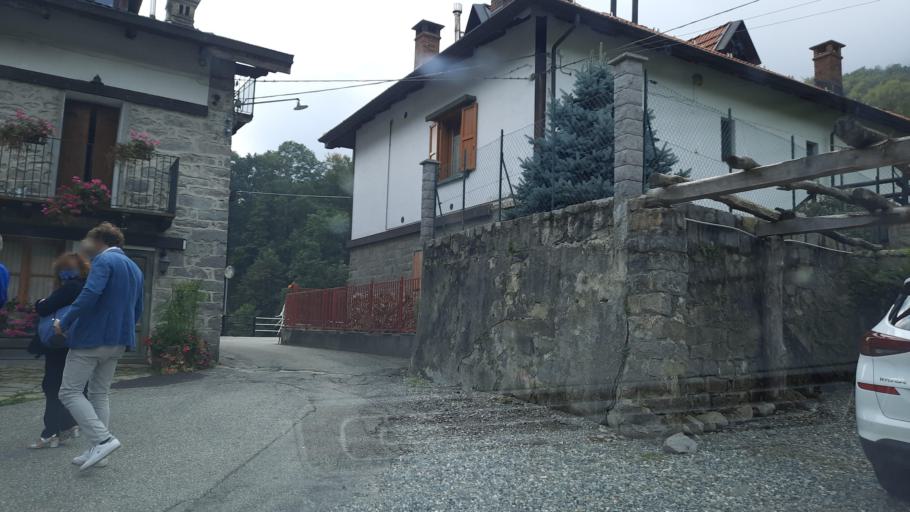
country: IT
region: Piedmont
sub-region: Provincia di Biella
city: Campiglia Cervo
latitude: 45.6586
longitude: 8.0021
